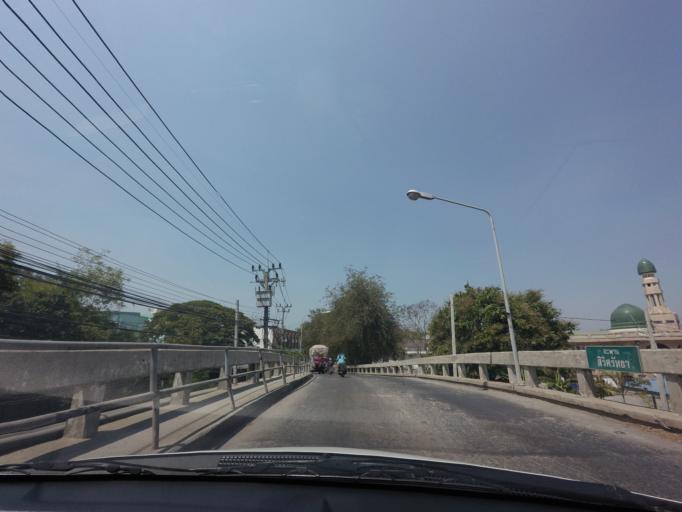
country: TH
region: Bangkok
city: Nong Chok
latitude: 13.8578
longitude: 100.8542
